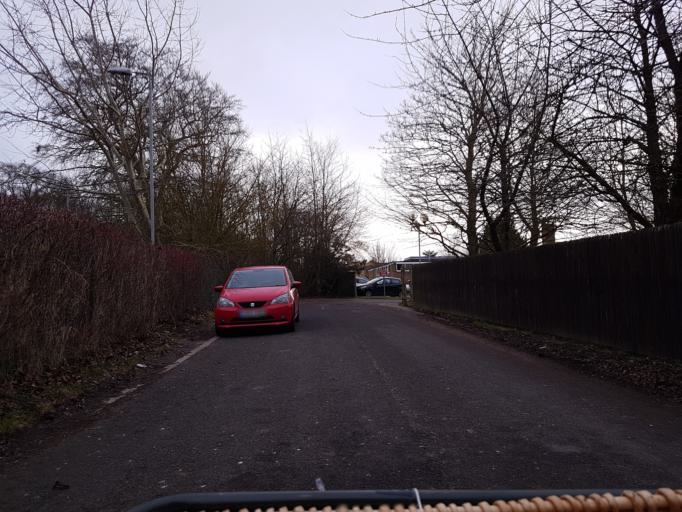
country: GB
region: England
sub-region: Cambridgeshire
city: Fulbourn
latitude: 52.1864
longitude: 0.1906
